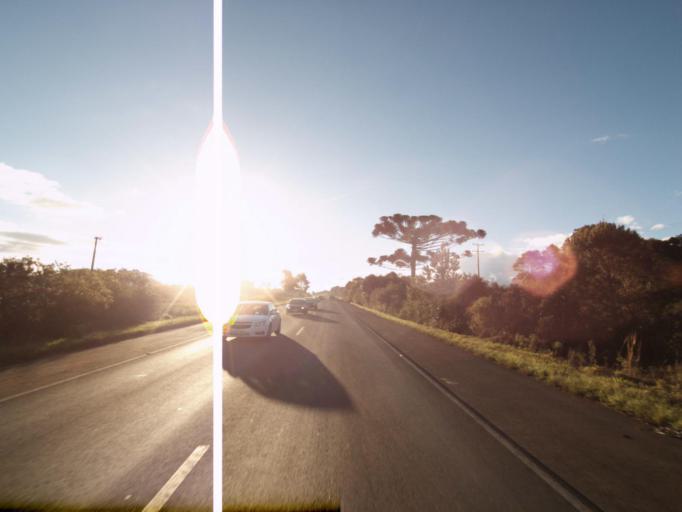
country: BR
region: Santa Catarina
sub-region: Campos Novos
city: Campos Novos
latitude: -27.3725
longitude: -51.2494
